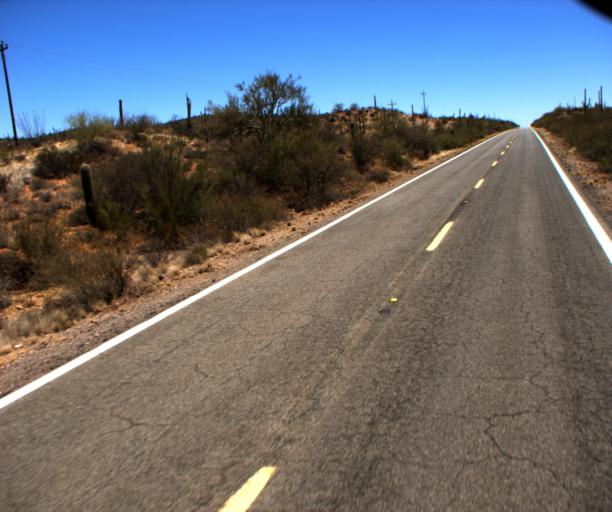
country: US
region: Arizona
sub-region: Pima County
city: Sells
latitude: 32.1747
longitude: -112.1784
